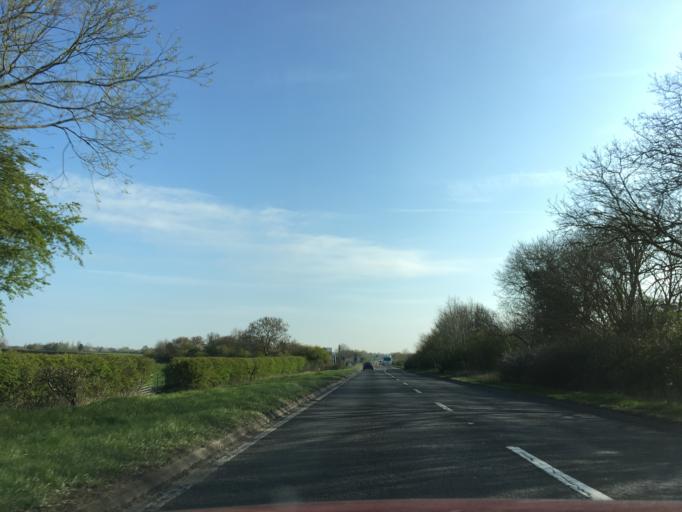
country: GB
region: England
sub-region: Northamptonshire
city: Deanshanger
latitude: 52.0410
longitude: -0.8889
